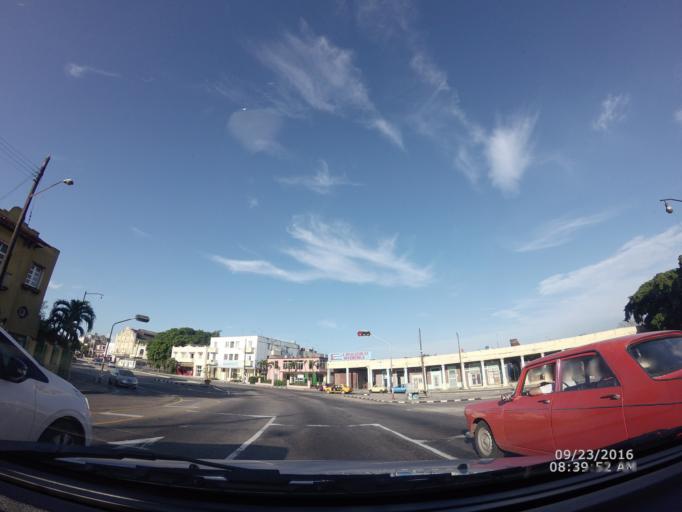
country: CU
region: La Habana
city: Havana
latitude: 23.1154
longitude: -82.4123
